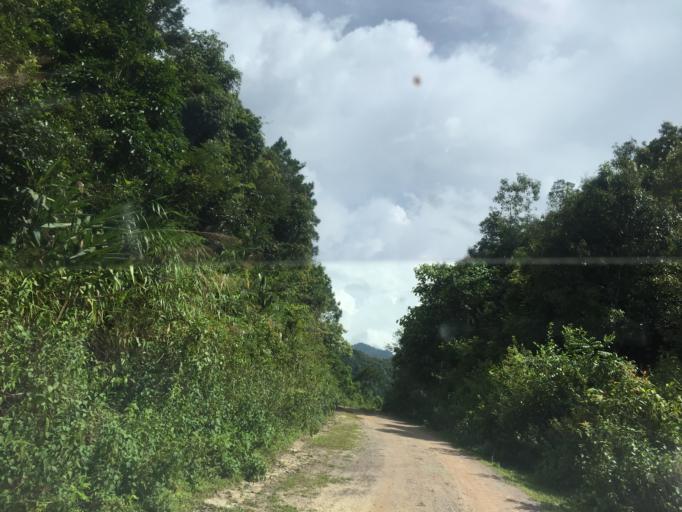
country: LA
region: Xiangkhoang
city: Muang Phonsavan
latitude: 19.3382
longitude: 103.5169
